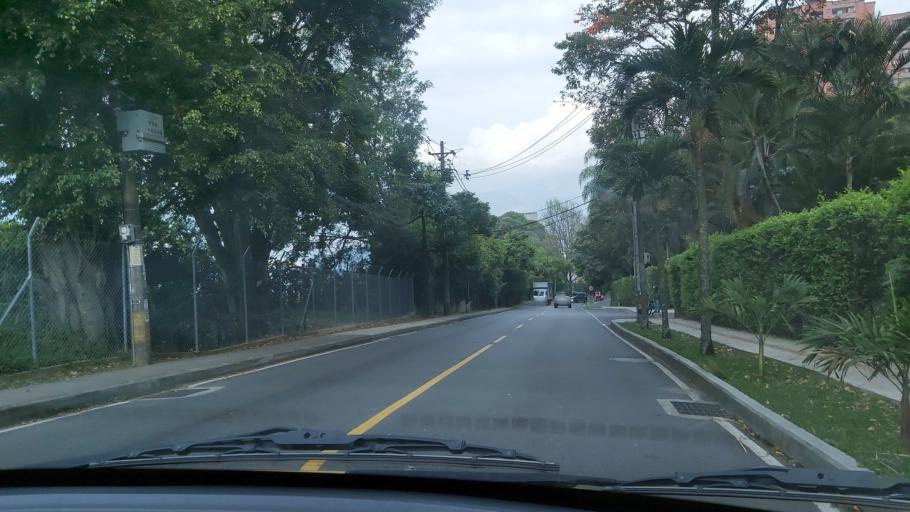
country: CO
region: Antioquia
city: Medellin
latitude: 6.2264
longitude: -75.5615
